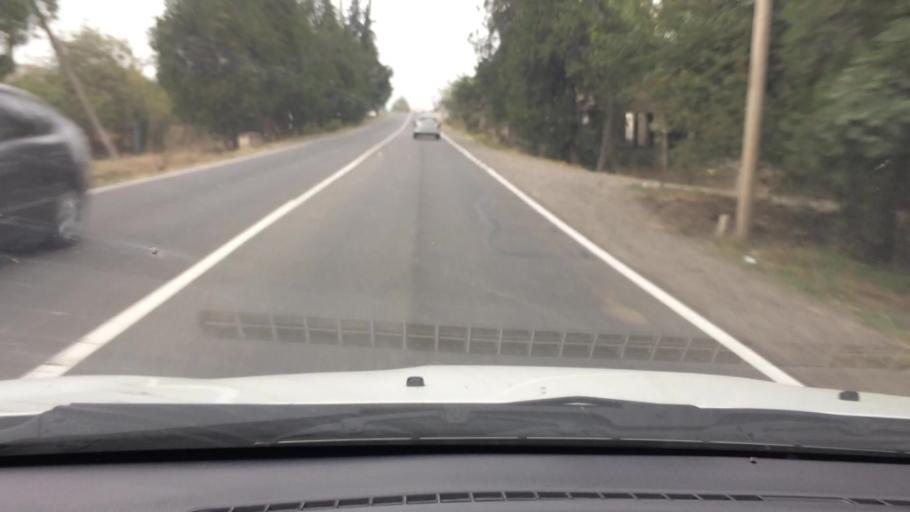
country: GE
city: Naghvarevi
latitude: 41.3701
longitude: 44.8370
